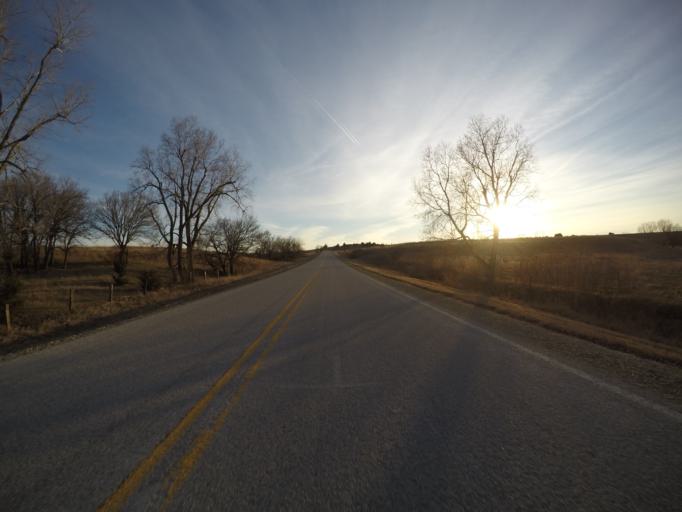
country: US
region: Kansas
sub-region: Riley County
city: Ogden
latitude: 39.3002
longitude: -96.7522
